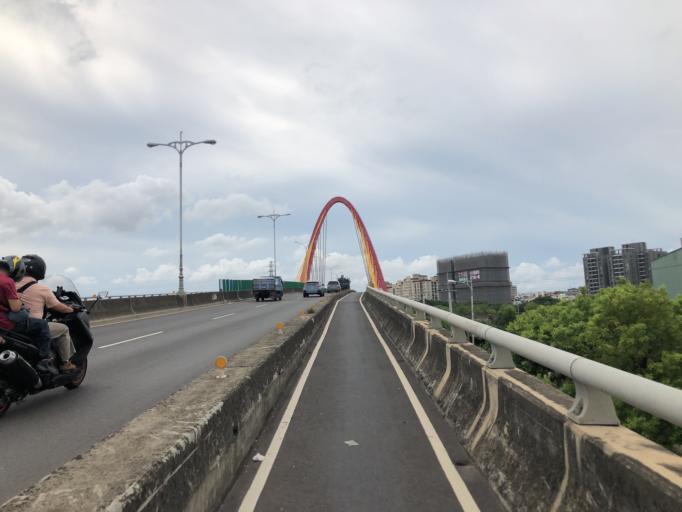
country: TW
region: Taiwan
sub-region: Changhua
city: Chang-hua
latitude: 24.0973
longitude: 120.6271
